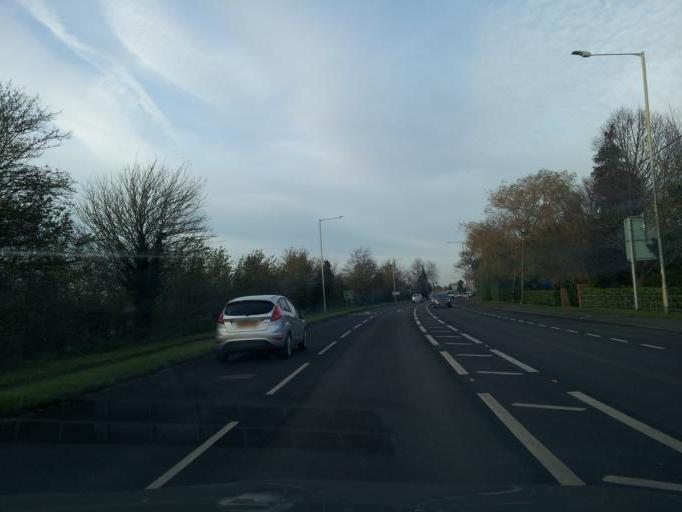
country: GB
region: England
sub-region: Buckinghamshire
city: Weston Turville
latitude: 51.7871
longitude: -0.7778
